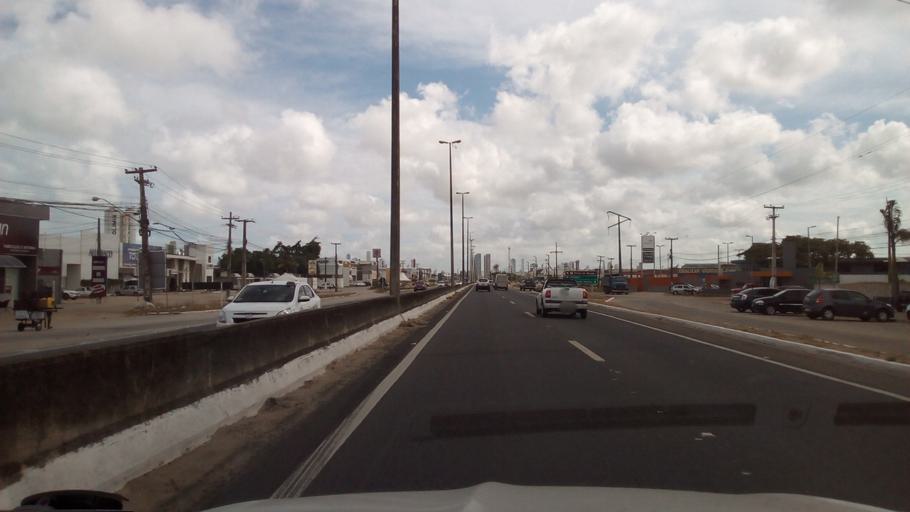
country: BR
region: Paraiba
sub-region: Joao Pessoa
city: Joao Pessoa
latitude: -7.0692
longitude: -34.8499
